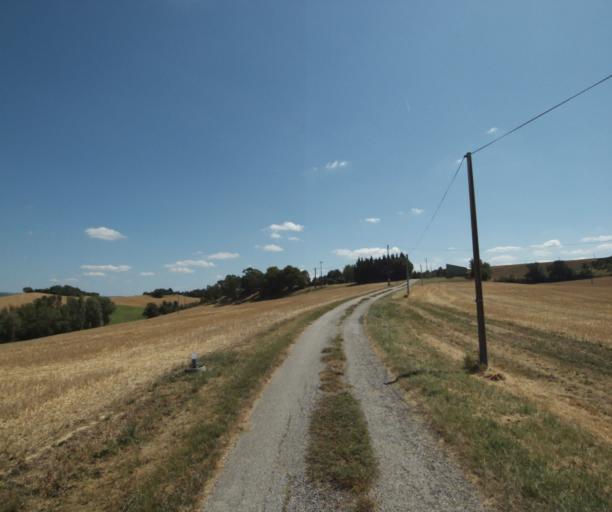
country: FR
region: Midi-Pyrenees
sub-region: Departement de la Haute-Garonne
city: Saint-Felix-Lauragais
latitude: 43.4610
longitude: 1.8849
